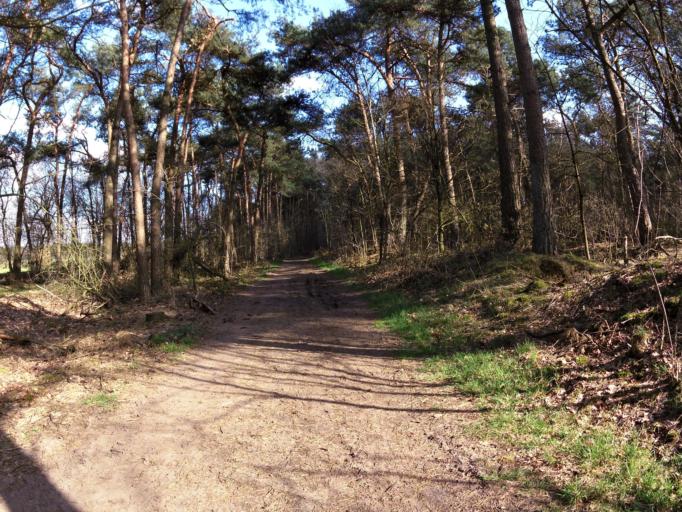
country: NL
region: North Brabant
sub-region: Gemeente Haaren
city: Haaren
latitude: 51.6572
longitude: 5.1663
